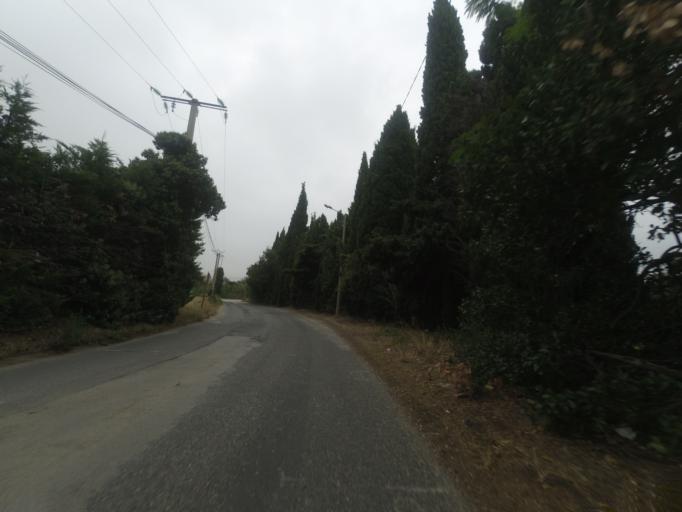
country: FR
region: Languedoc-Roussillon
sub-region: Departement des Pyrenees-Orientales
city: Baho
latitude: 42.6963
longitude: 2.8240
